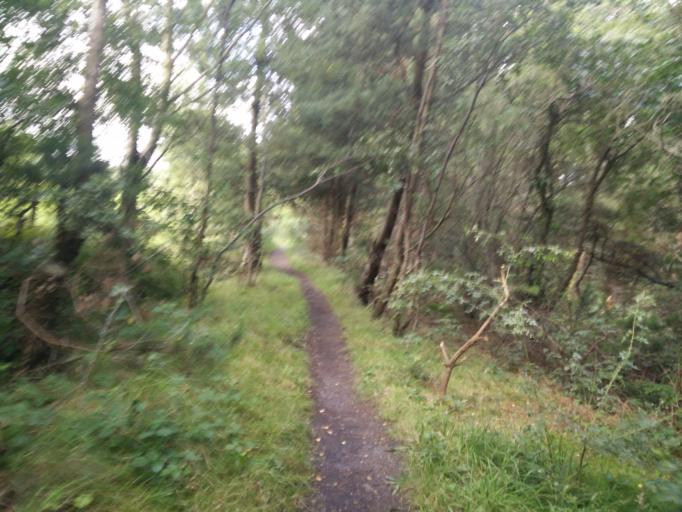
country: GB
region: England
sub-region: County Durham
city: Crook
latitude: 54.7225
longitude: -1.7613
